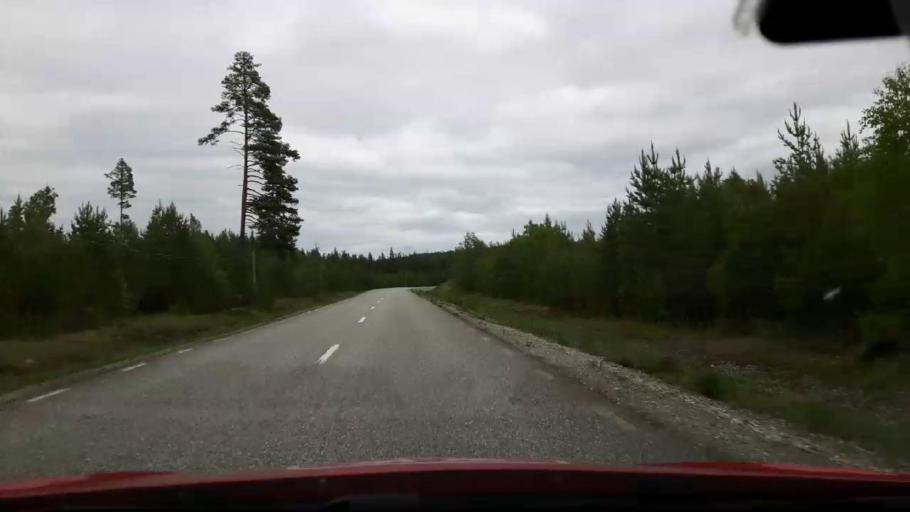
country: SE
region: Jaemtland
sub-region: Ragunda Kommun
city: Hammarstrand
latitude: 63.2646
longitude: 15.8743
